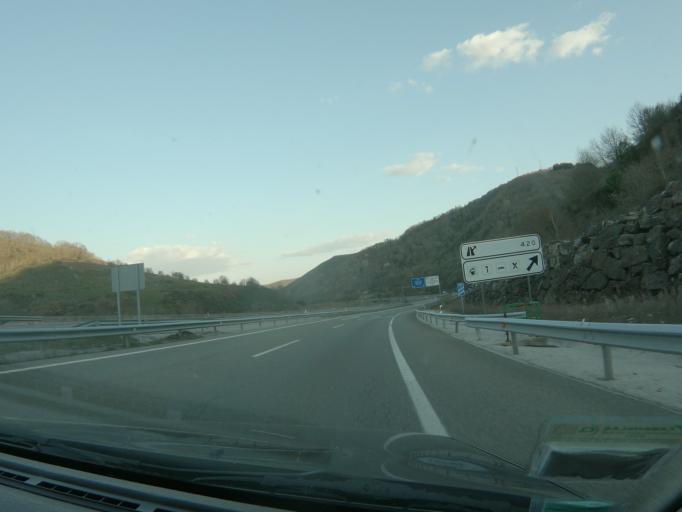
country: ES
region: Castille and Leon
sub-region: Provincia de Leon
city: Vega de Valcarce
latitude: 42.6632
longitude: -6.9295
